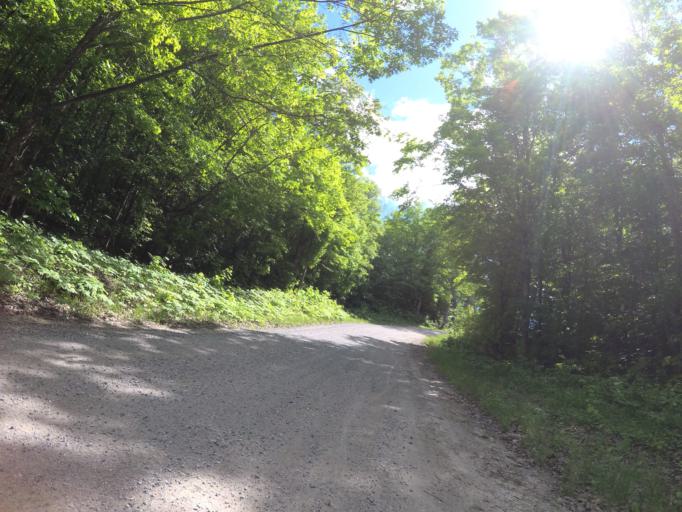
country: CA
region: Ontario
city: Renfrew
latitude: 45.0436
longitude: -76.8208
